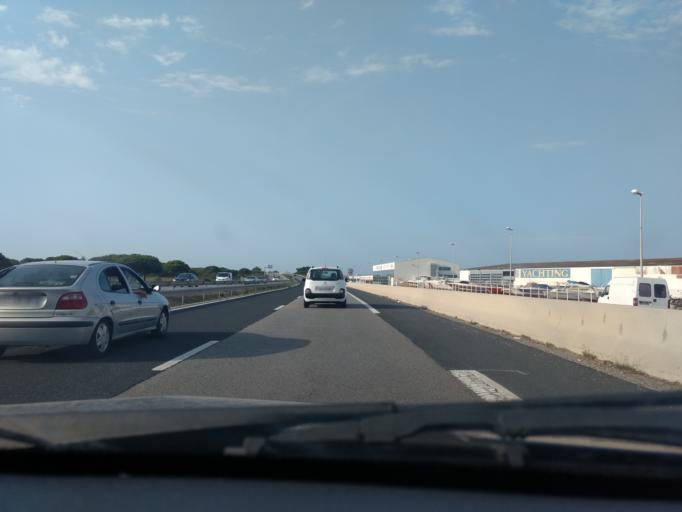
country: FR
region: Languedoc-Roussillon
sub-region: Departement des Pyrenees-Orientales
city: Le Barcares
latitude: 42.8006
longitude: 3.0296
